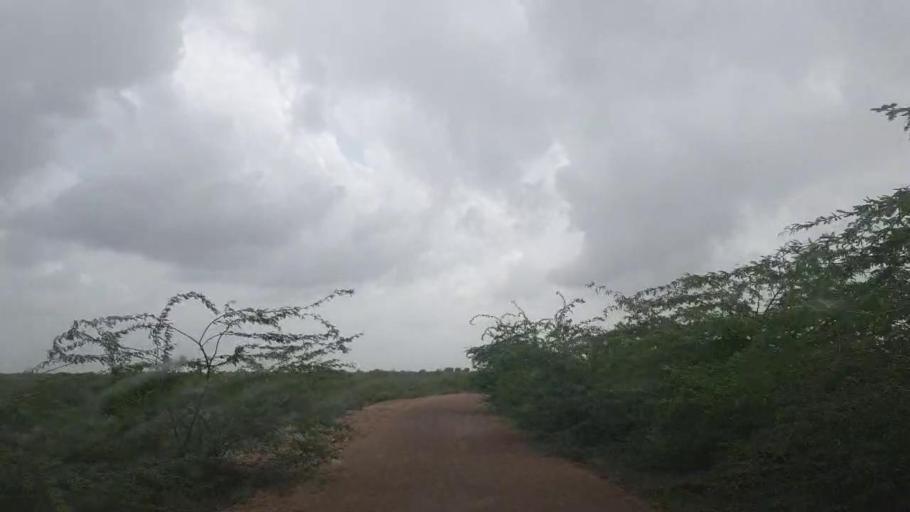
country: PK
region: Sindh
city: Naukot
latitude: 24.8684
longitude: 69.2266
